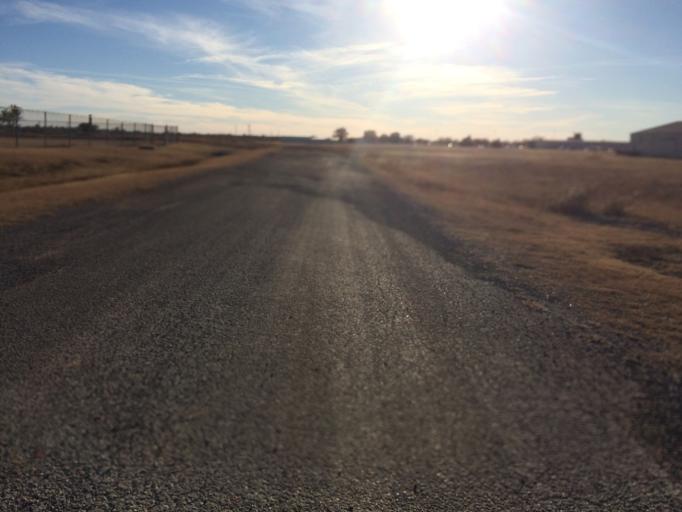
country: US
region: Oklahoma
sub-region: Cleveland County
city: Norman
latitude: 35.2437
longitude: -97.4624
